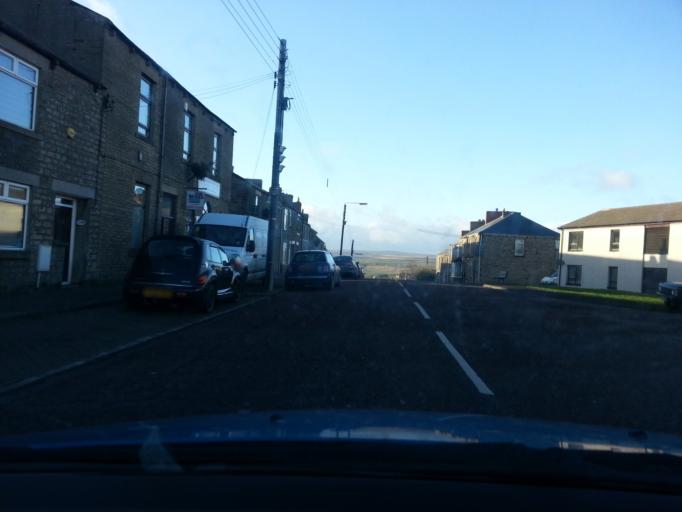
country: GB
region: England
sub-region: County Durham
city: Tow Law
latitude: 54.7423
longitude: -1.8146
